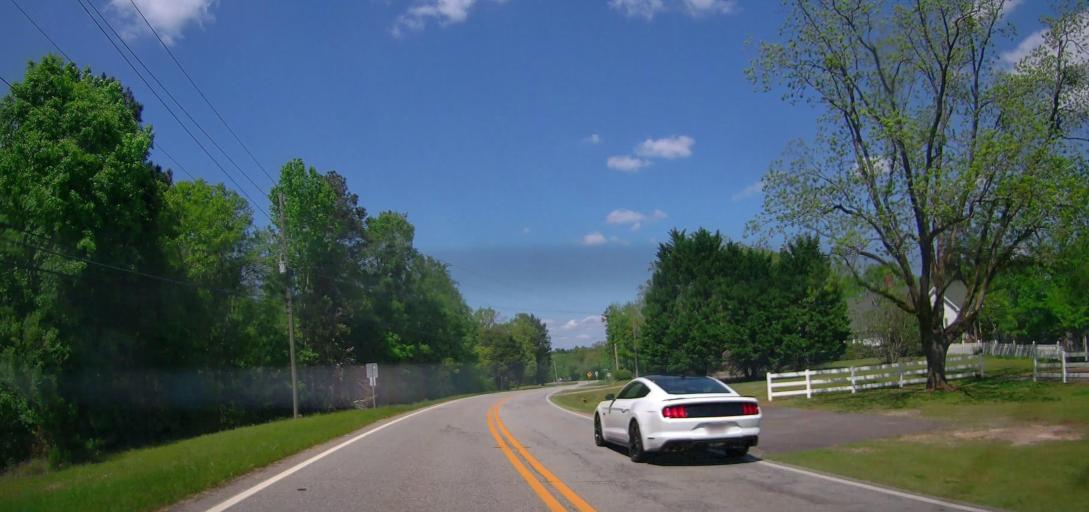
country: US
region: Georgia
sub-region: Putnam County
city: Eatonton
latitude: 33.3040
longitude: -83.3030
